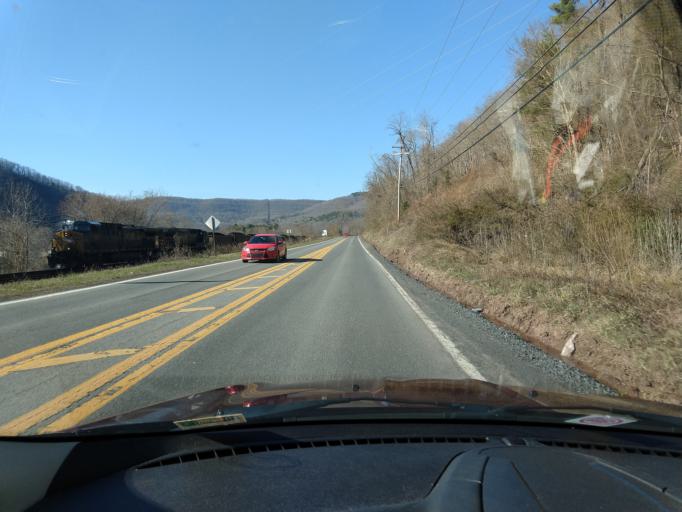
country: US
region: West Virginia
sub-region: Summers County
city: Hinton
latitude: 37.7091
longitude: -80.8875
